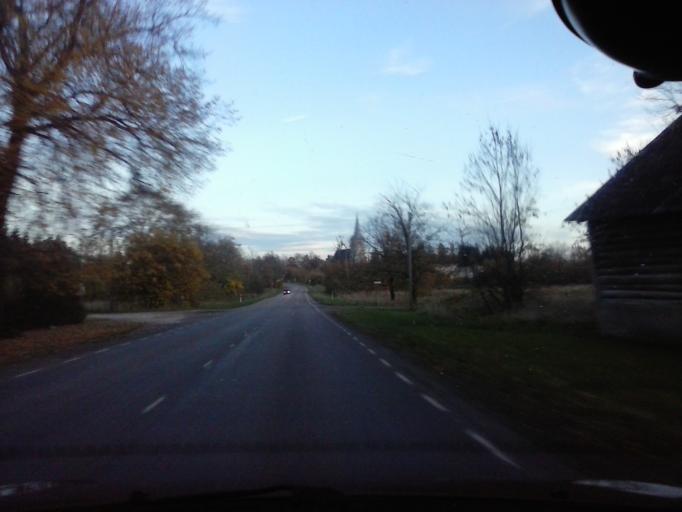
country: EE
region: Raplamaa
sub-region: Maerjamaa vald
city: Marjamaa
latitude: 58.9144
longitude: 24.4248
